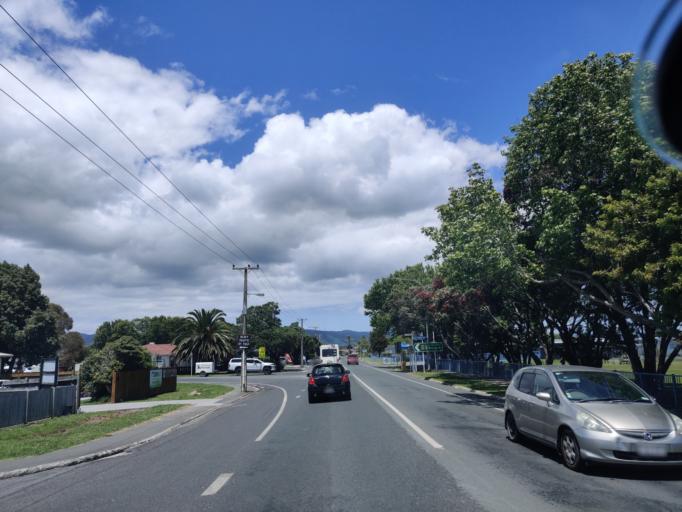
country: NZ
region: Northland
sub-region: Far North District
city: Kaitaia
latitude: -35.1029
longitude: 173.2592
